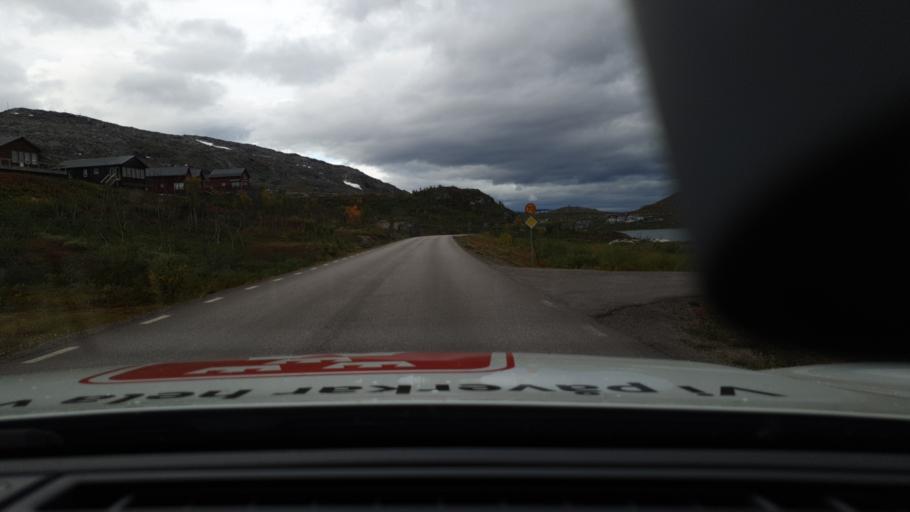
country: NO
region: Troms
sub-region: Bardu
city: Setermoen
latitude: 68.4260
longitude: 18.1616
